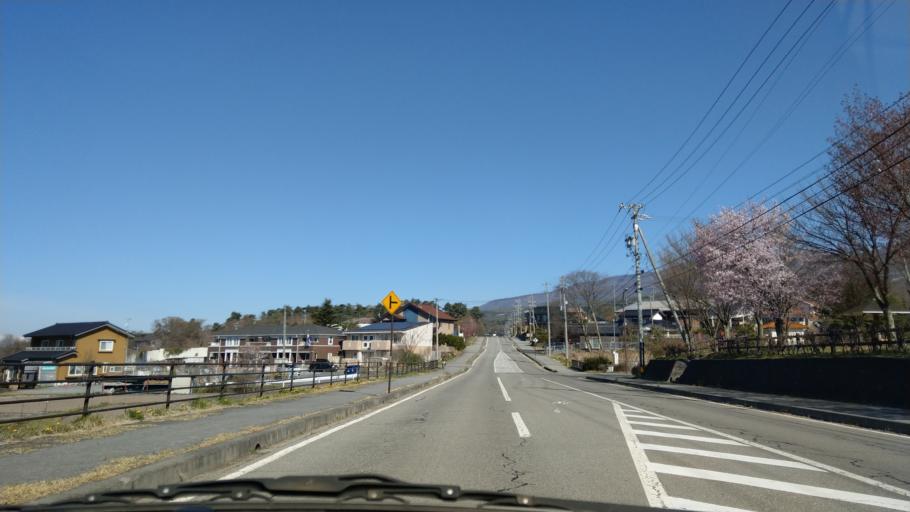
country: JP
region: Nagano
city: Komoro
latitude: 36.3296
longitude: 138.5031
